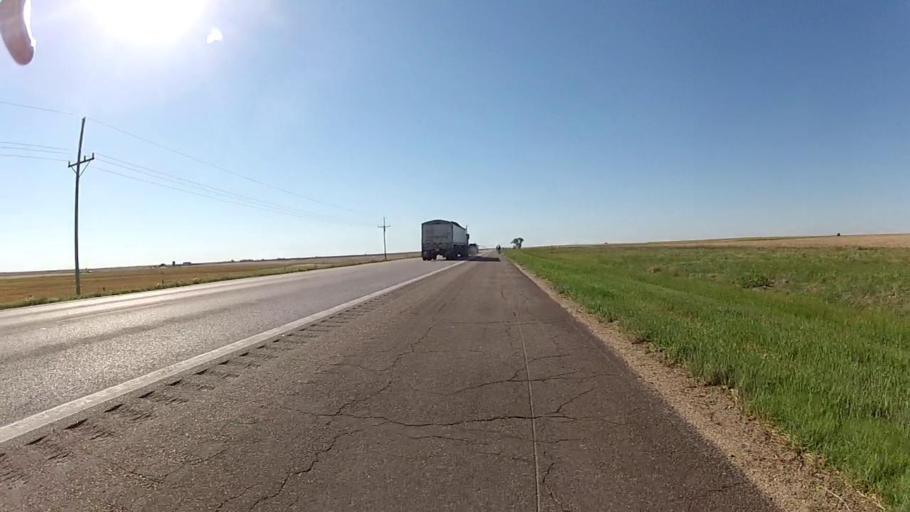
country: US
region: Kansas
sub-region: Ford County
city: Dodge City
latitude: 37.5964
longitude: -99.6960
